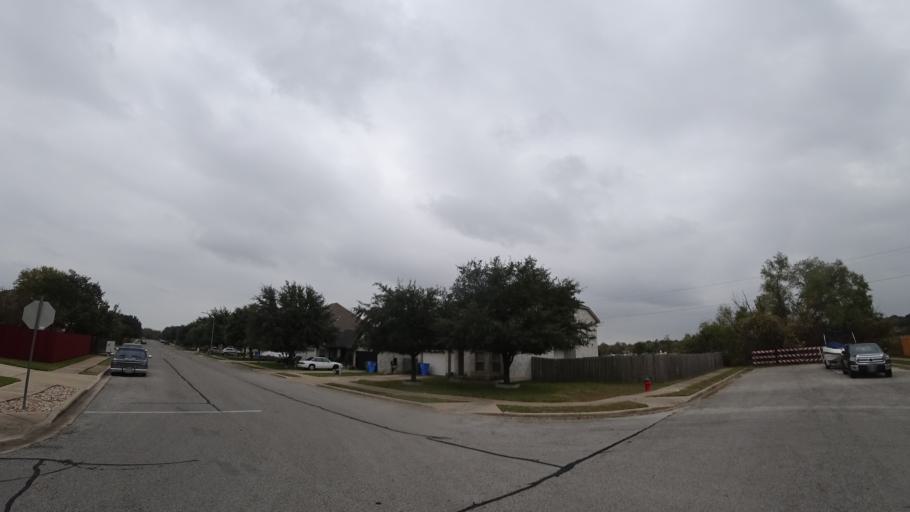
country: US
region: Texas
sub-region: Travis County
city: Pflugerville
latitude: 30.4244
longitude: -97.6212
